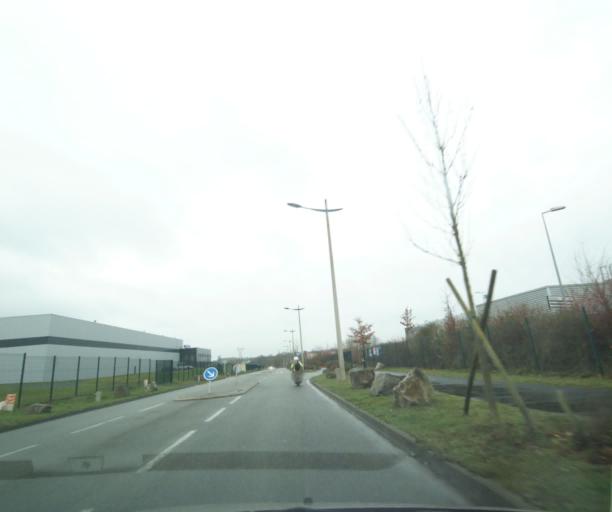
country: FR
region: Nord-Pas-de-Calais
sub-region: Departement du Nord
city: Haulchin
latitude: 50.3311
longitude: 3.4371
